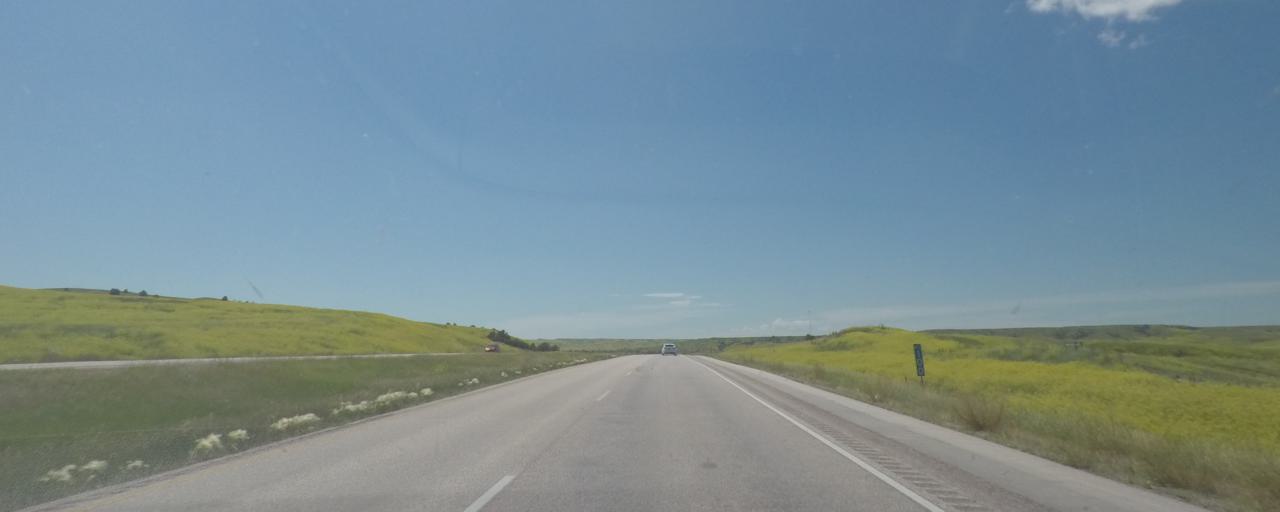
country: US
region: South Dakota
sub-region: Pennington County
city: Box Elder
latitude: 44.0687
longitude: -102.4105
